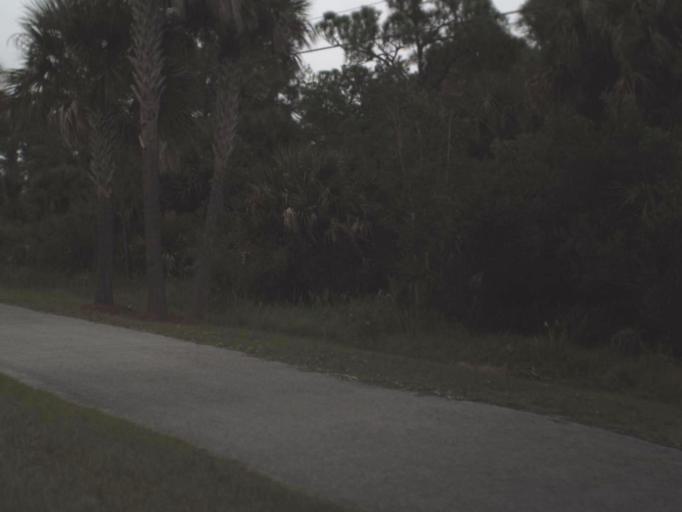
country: US
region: Florida
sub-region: Brevard County
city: Palm Bay
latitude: 28.0382
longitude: -80.5971
